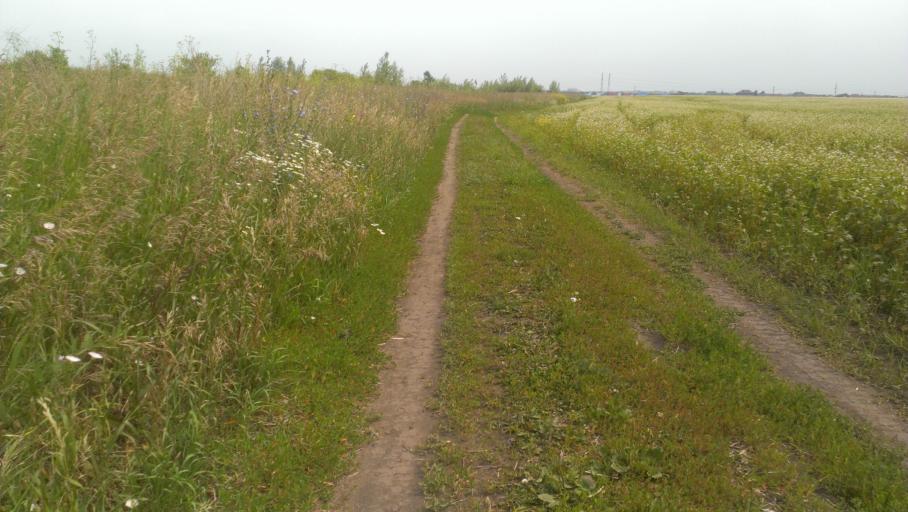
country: RU
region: Altai Krai
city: Novosilikatnyy
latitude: 53.3772
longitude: 83.6397
